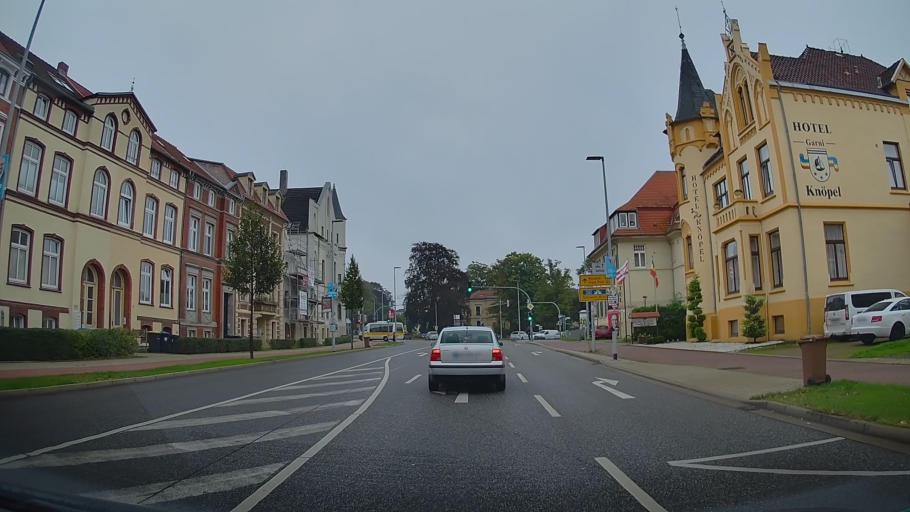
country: DE
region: Mecklenburg-Vorpommern
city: Wismar
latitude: 53.8884
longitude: 11.4612
